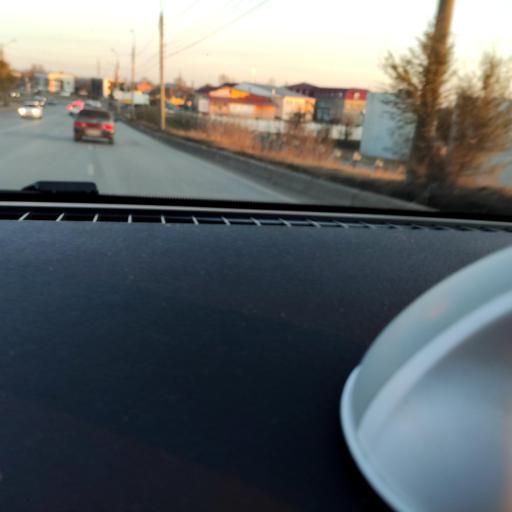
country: RU
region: Samara
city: Petra-Dubrava
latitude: 53.2546
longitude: 50.3071
